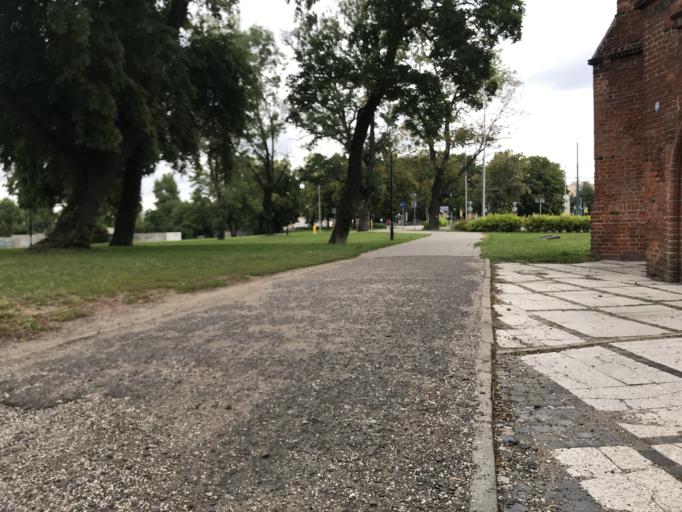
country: PL
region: Warmian-Masurian Voivodeship
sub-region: Powiat elblaski
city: Elblag
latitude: 54.1653
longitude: 19.3986
